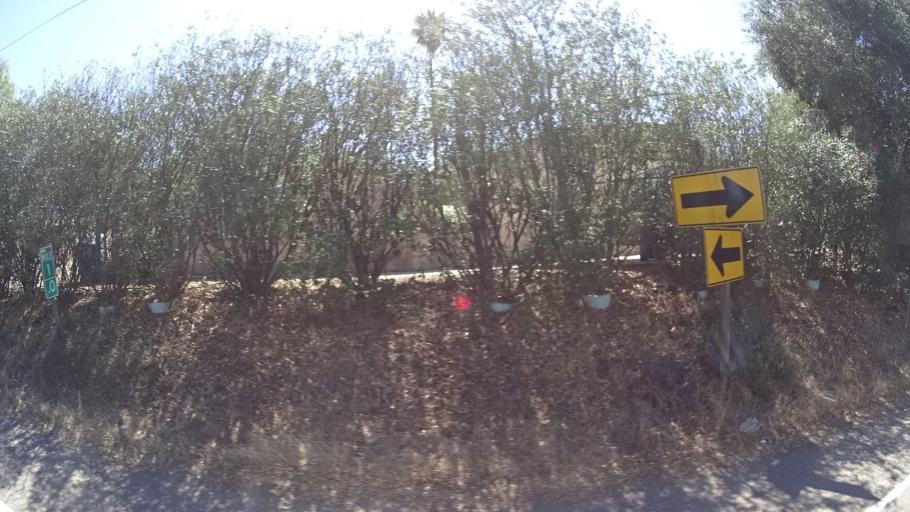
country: US
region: California
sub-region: San Diego County
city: Ramona
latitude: 33.0402
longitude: -116.8456
